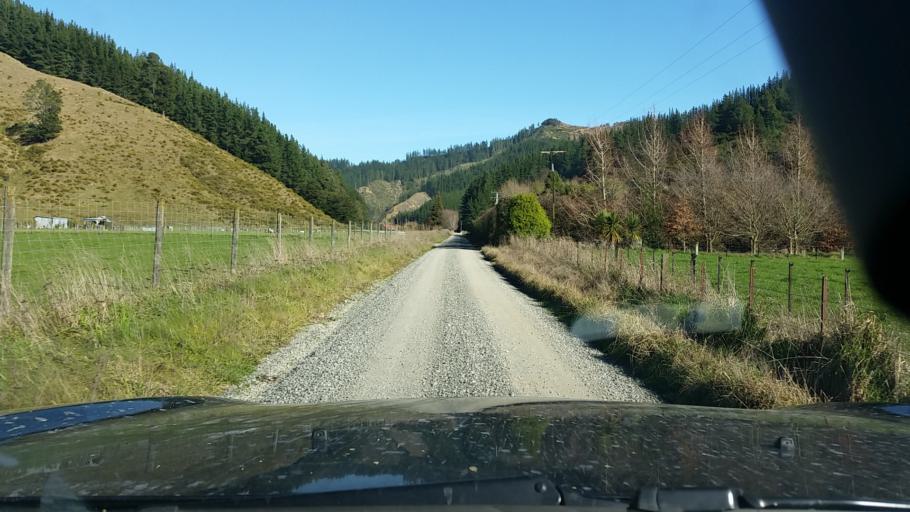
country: NZ
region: Marlborough
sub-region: Marlborough District
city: Blenheim
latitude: -41.4310
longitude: 173.7642
